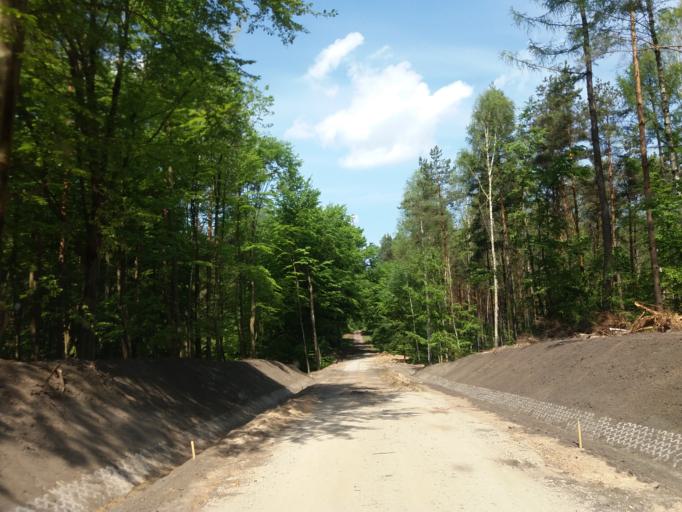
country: PL
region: West Pomeranian Voivodeship
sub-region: Powiat choszczenski
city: Bierzwnik
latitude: 53.0226
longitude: 15.6052
